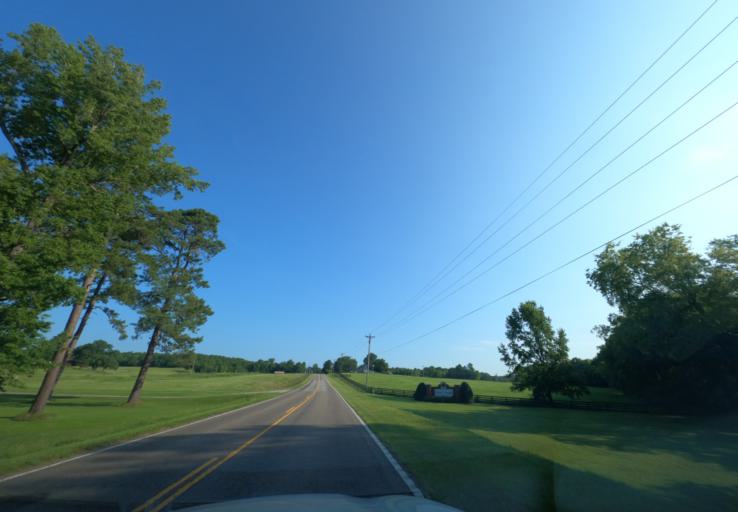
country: US
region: South Carolina
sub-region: Edgefield County
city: Murphys Estates
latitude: 33.6621
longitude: -81.9745
